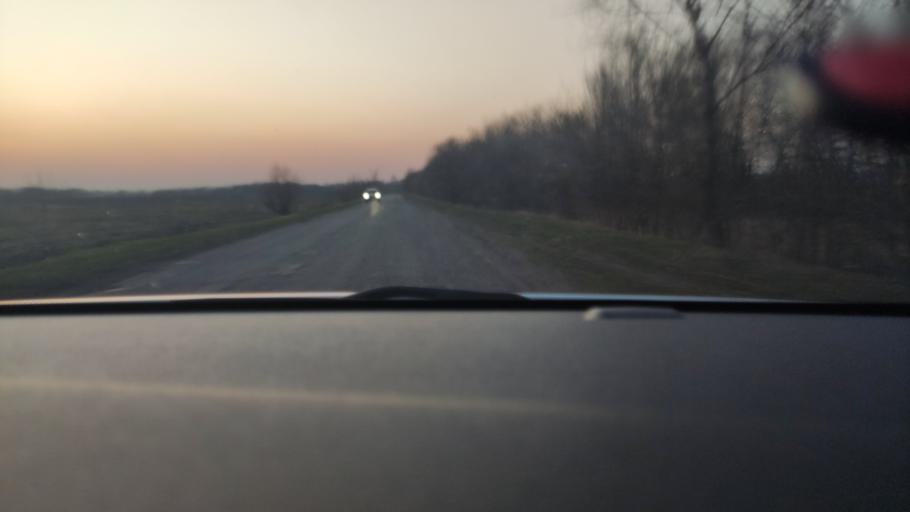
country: RU
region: Voronezj
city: Uryv-Pokrovka
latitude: 51.1174
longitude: 39.1410
